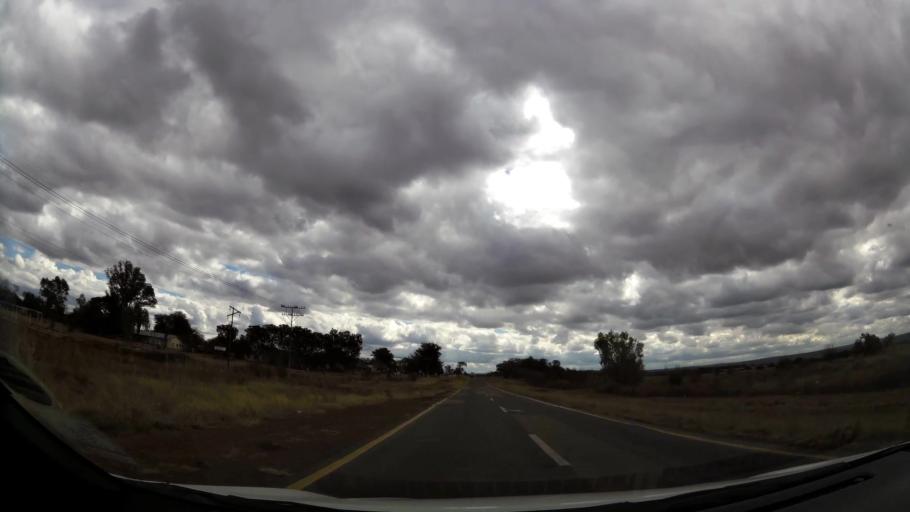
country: ZA
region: Limpopo
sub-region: Waterberg District Municipality
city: Modimolle
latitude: -24.7458
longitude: 28.4416
